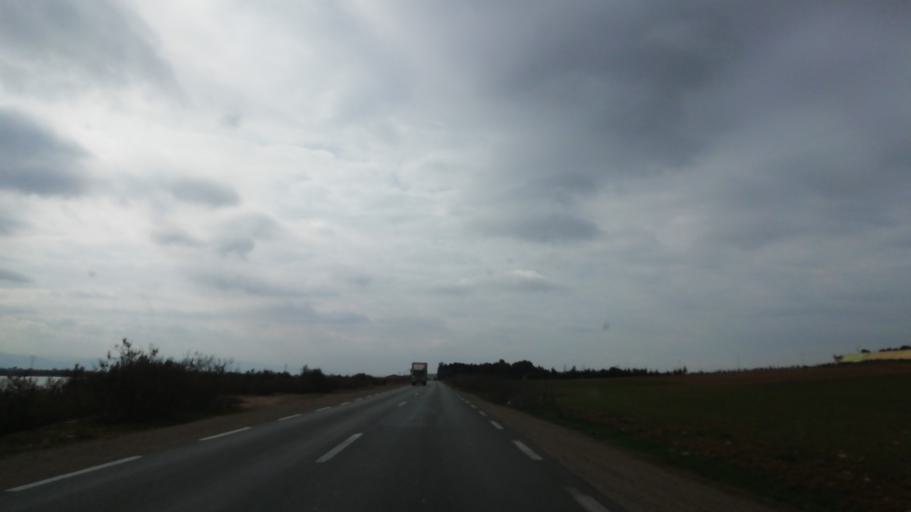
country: DZ
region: Oran
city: Sidi ech Chahmi
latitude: 35.6045
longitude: -0.4358
